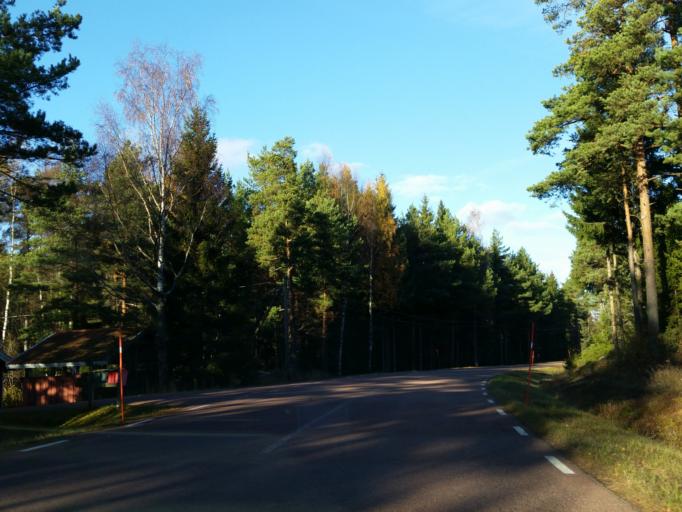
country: AX
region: Alands landsbygd
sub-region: Finstroem
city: Finstroem
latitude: 60.3167
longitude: 19.9410
